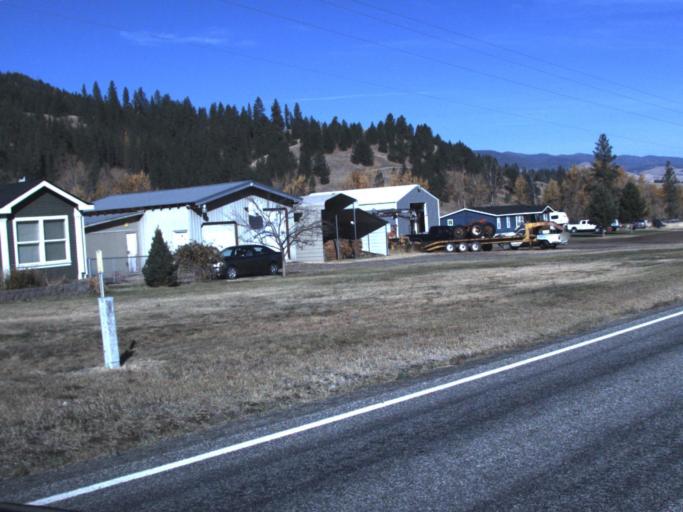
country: US
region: Washington
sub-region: Ferry County
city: Republic
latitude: 48.8154
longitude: -118.5992
